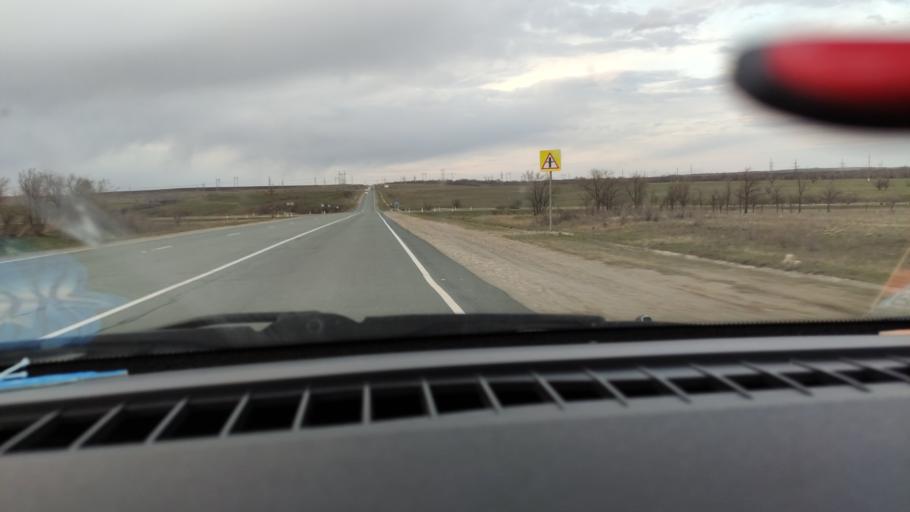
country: RU
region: Saratov
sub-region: Saratovskiy Rayon
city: Saratov
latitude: 51.7573
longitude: 46.0675
